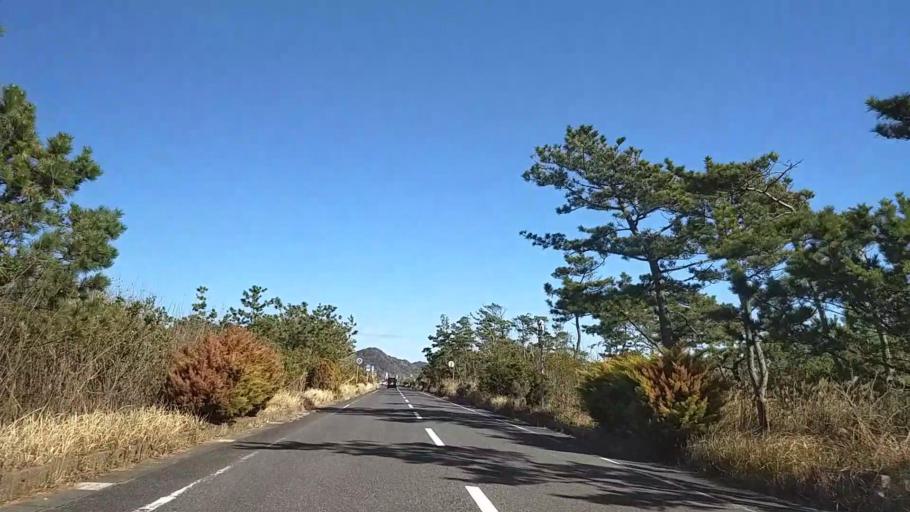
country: JP
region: Chiba
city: Tateyama
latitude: 35.0174
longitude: 139.9856
